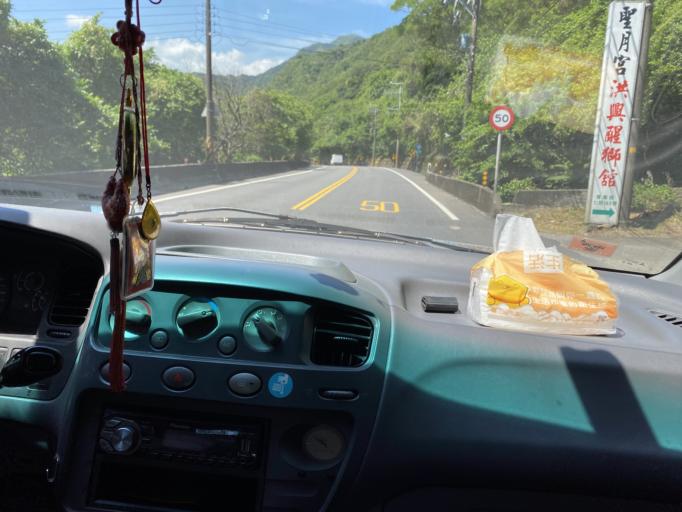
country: TW
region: Taiwan
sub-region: Keelung
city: Keelung
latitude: 24.9752
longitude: 121.9376
